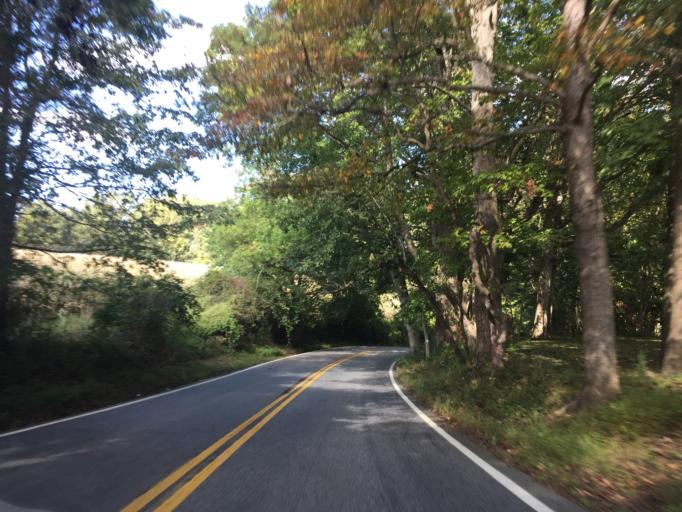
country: US
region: Maryland
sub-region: Harford County
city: Fallston
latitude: 39.5042
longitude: -76.4633
